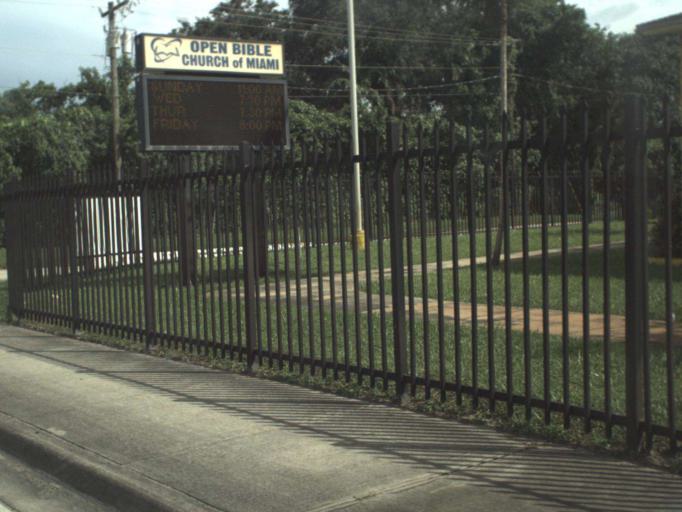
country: US
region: Florida
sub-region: Miami-Dade County
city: Westview
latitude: 25.8826
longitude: -80.2413
